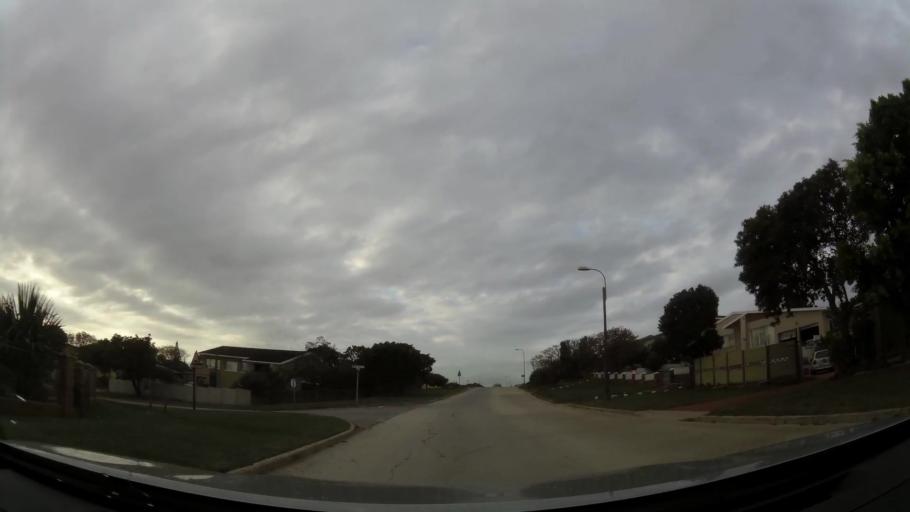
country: ZA
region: Eastern Cape
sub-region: Nelson Mandela Bay Metropolitan Municipality
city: Port Elizabeth
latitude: -33.9374
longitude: 25.5480
